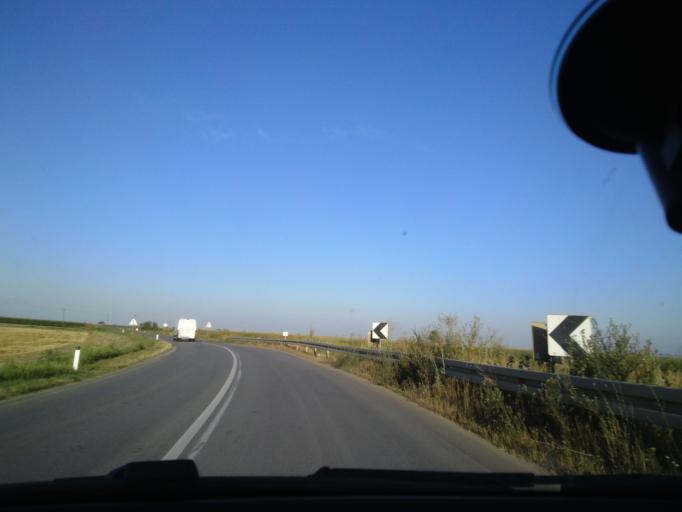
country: RS
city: Obrovac
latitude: 45.4095
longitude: 19.4075
